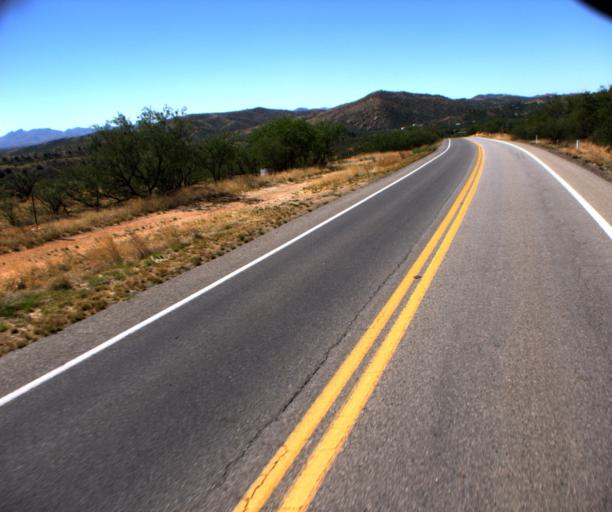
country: US
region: Arizona
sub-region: Santa Cruz County
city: Nogales
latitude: 31.4052
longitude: -110.8665
